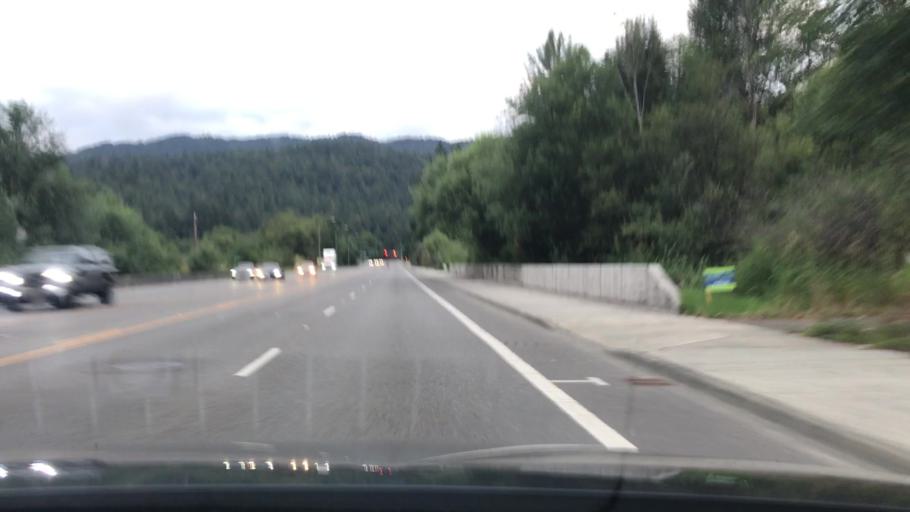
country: US
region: Washington
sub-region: King County
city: Issaquah
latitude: 47.5360
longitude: -122.0629
